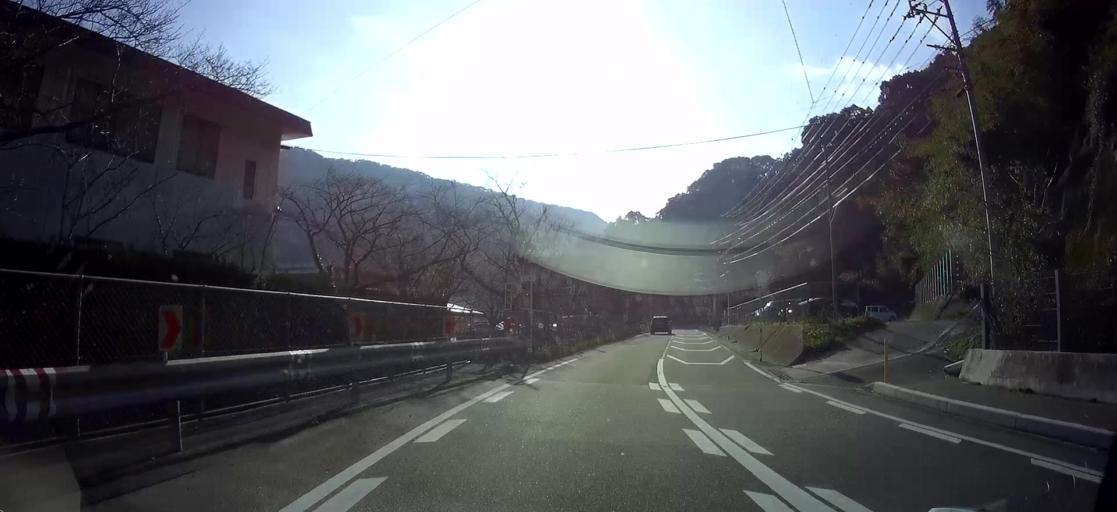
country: JP
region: Kumamoto
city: Minamata
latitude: 32.4191
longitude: 130.4054
